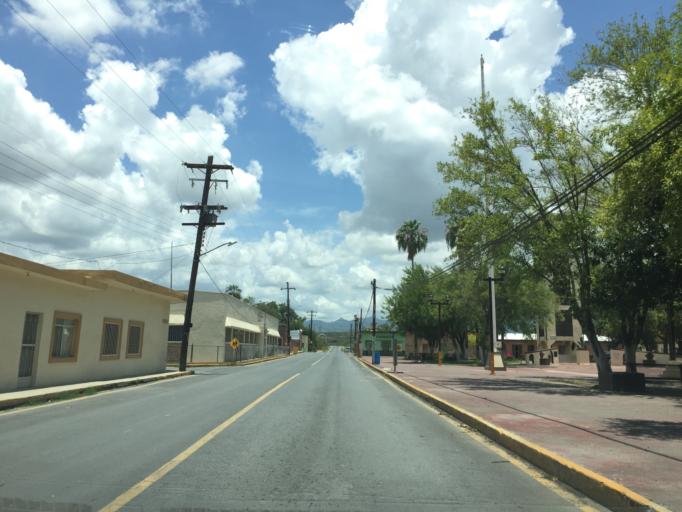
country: MX
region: Nuevo Leon
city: Marin
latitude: 25.8590
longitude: -99.9420
